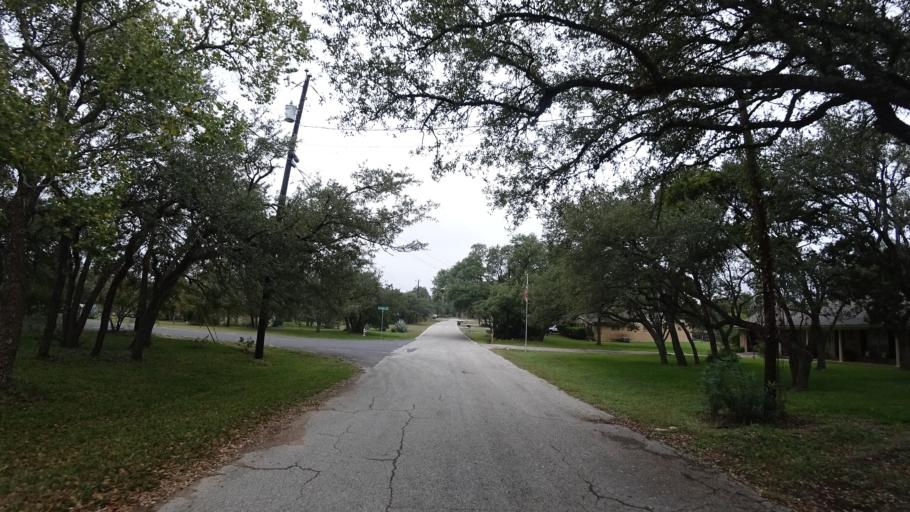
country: US
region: Texas
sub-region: Travis County
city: Barton Creek
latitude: 30.2284
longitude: -97.8947
